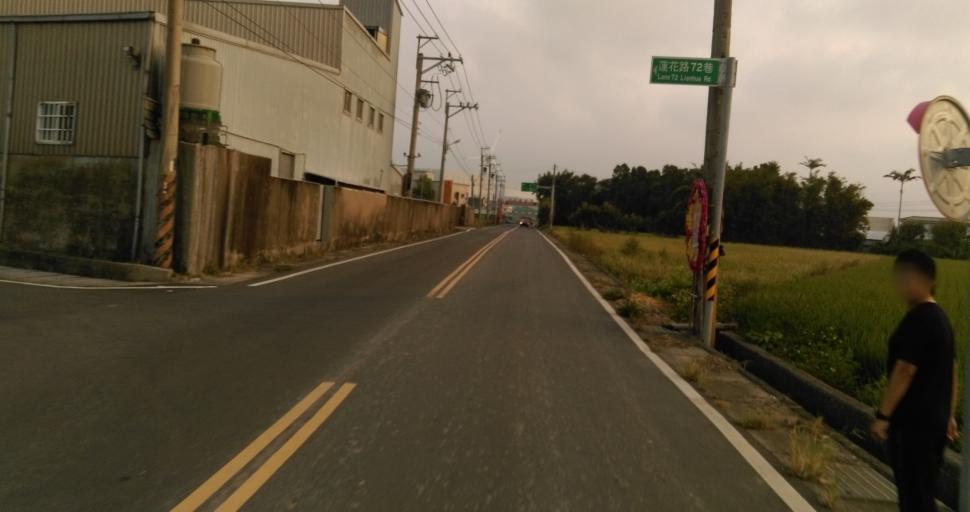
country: TW
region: Taiwan
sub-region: Hsinchu
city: Zhubei
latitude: 24.8636
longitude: 120.9604
